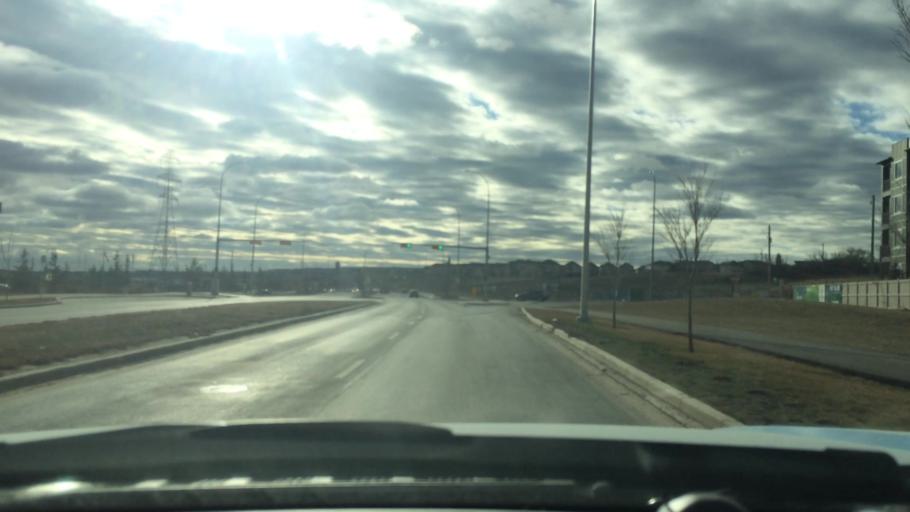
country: CA
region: Alberta
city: Calgary
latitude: 51.1707
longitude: -114.1335
